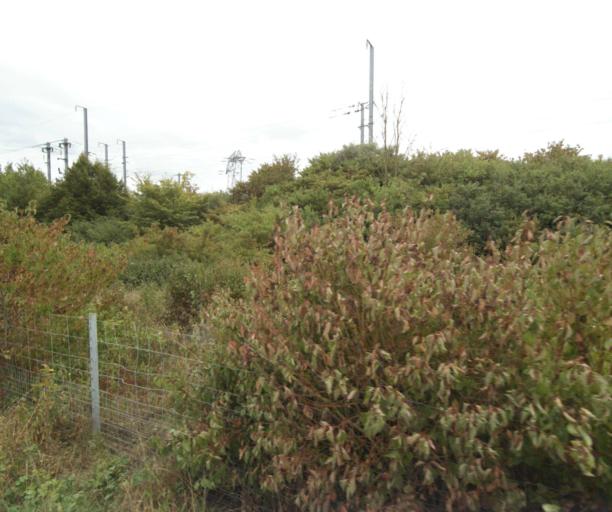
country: FR
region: Nord-Pas-de-Calais
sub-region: Departement du Nord
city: Sainghin-en-Melantois
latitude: 50.5711
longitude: 3.1608
